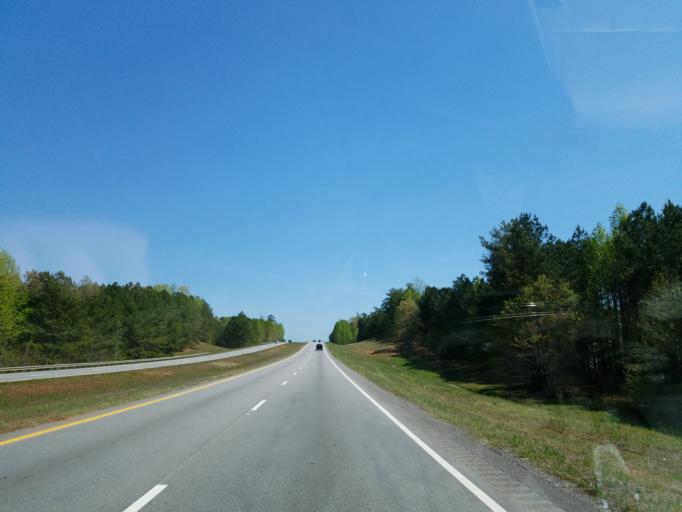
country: US
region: Georgia
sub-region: Paulding County
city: Dallas
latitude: 33.9064
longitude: -84.8173
